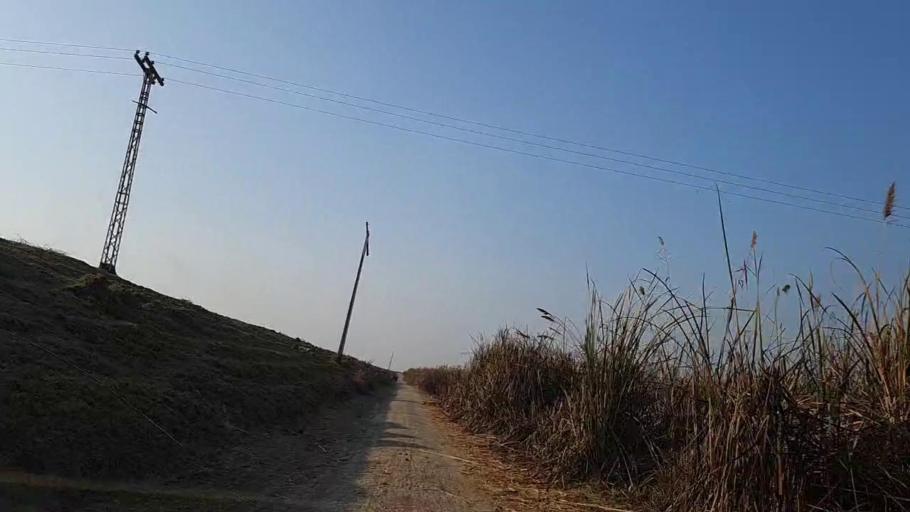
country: PK
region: Sindh
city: Sakrand
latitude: 26.0963
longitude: 68.3710
